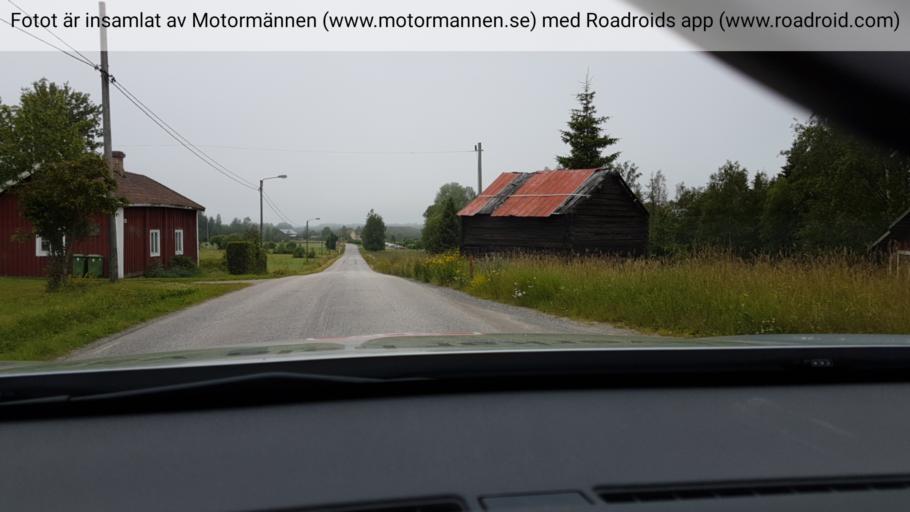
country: SE
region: Vaesternorrland
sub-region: Sundsvalls Kommun
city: Johannedal
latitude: 62.4316
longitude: 17.4547
